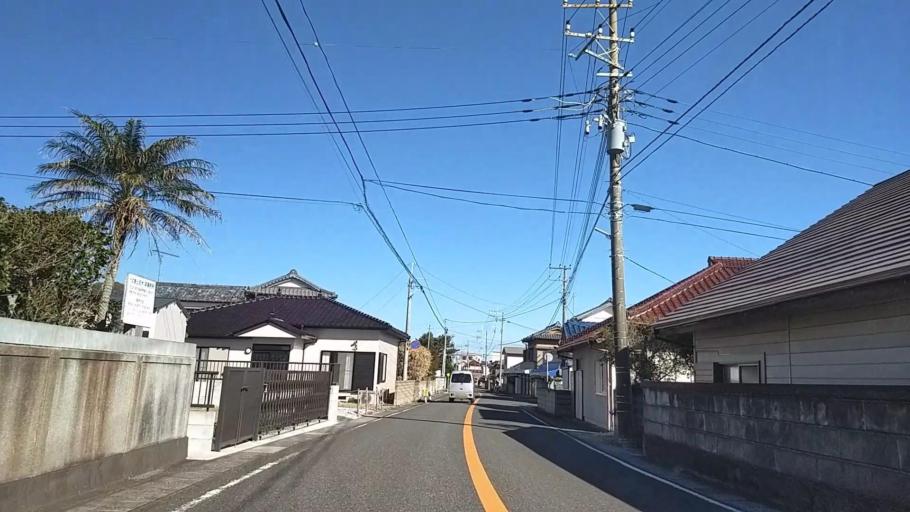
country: JP
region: Chiba
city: Tateyama
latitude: 34.9301
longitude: 139.9454
